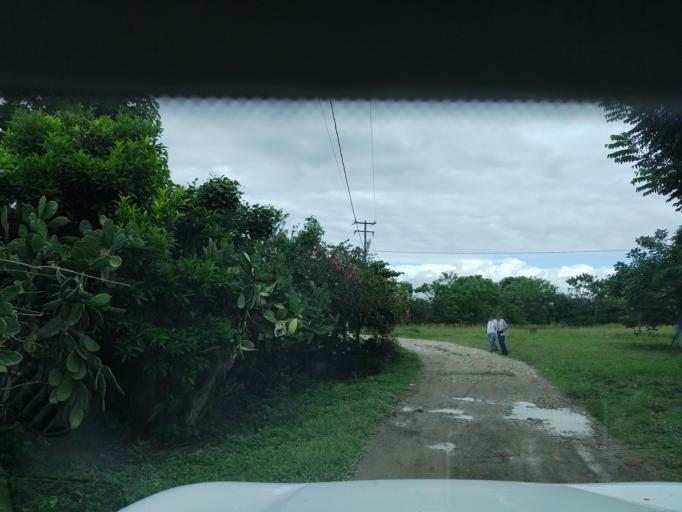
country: MX
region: Veracruz
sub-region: Atzalan
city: Colonias Pedernales
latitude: 20.0399
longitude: -97.0744
